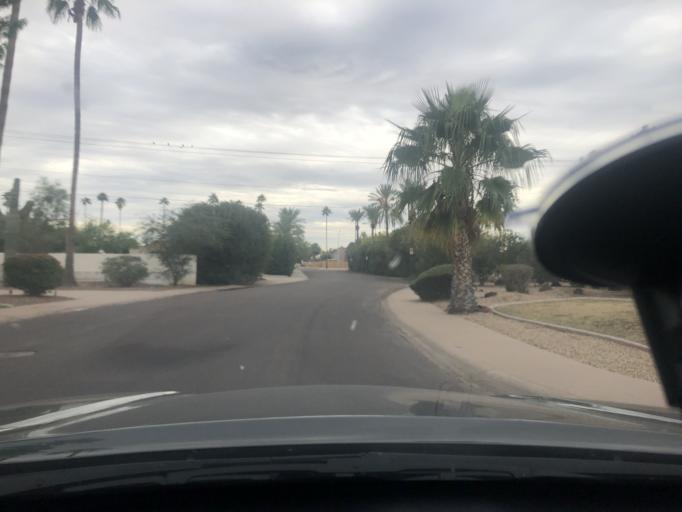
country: US
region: Arizona
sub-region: Maricopa County
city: Scottsdale
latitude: 33.4817
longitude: -111.9030
